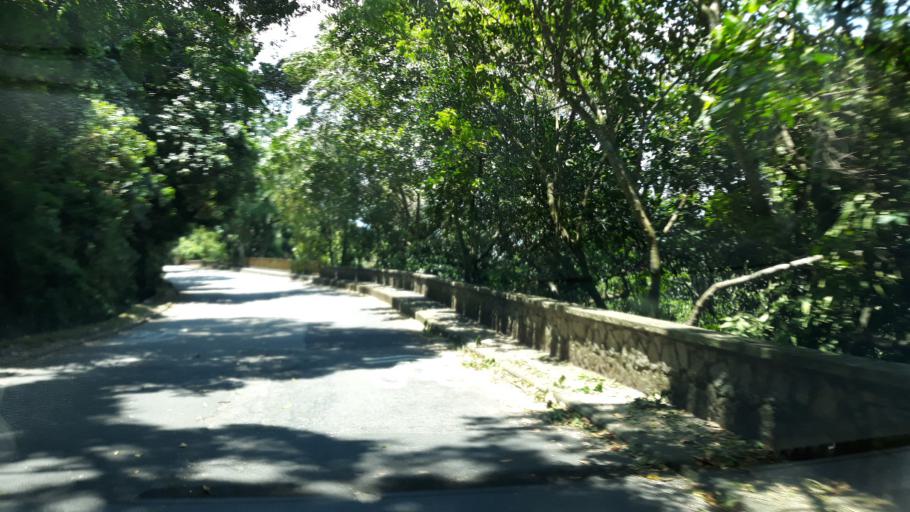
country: BR
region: Rio de Janeiro
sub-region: Rio De Janeiro
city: Rio de Janeiro
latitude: -22.9461
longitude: -43.2057
